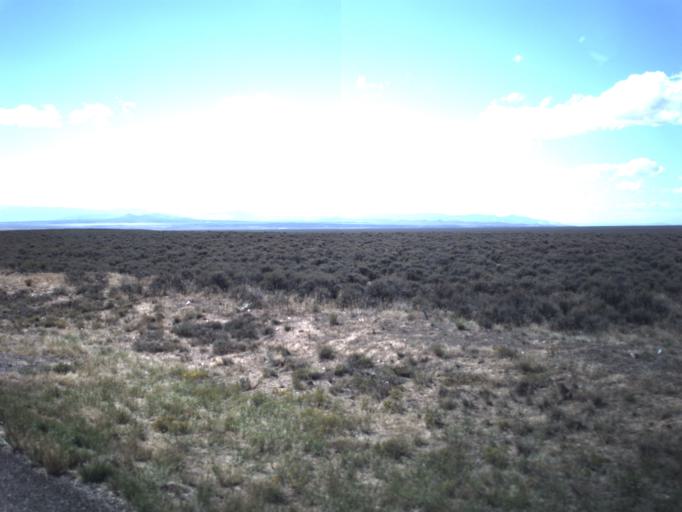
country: US
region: Utah
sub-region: Iron County
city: Enoch
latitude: 37.9658
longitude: -113.0074
